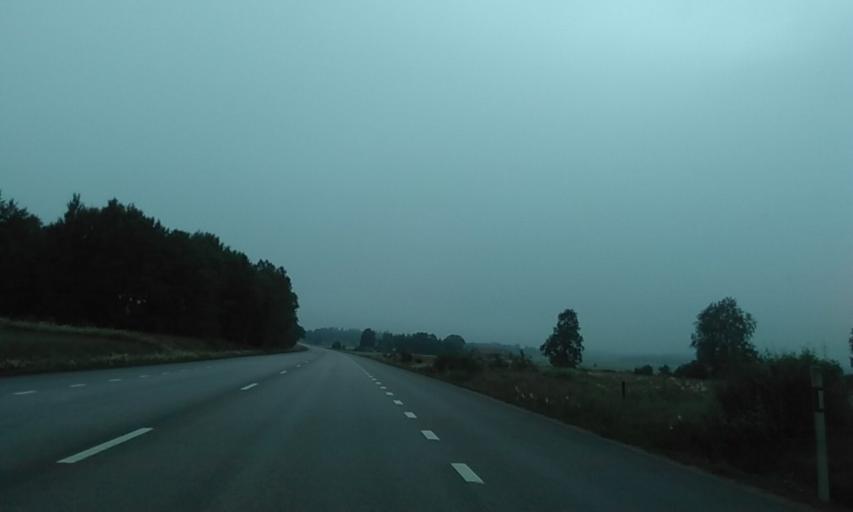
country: SE
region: Vaestra Goetaland
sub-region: Vargarda Kommun
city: Vargarda
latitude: 58.1292
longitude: 12.8566
